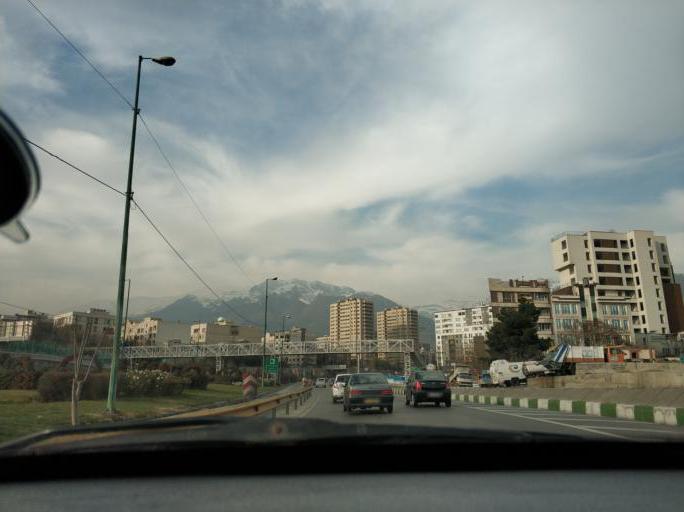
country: IR
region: Tehran
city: Tajrish
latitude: 35.7875
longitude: 51.4920
